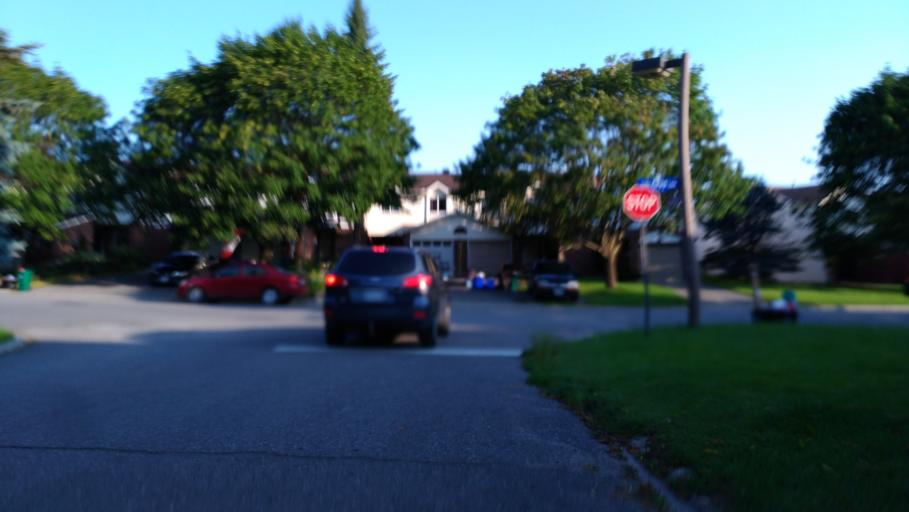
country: CA
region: Ontario
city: Bells Corners
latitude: 45.3483
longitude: -75.9281
